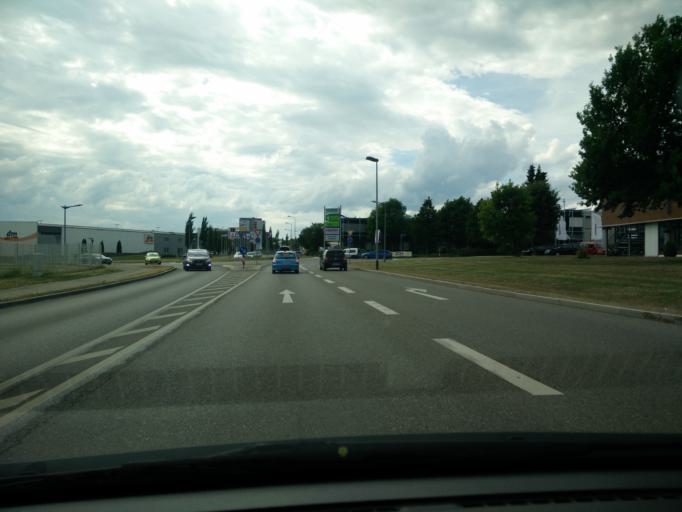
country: DE
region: Baden-Wuerttemberg
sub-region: Freiburg Region
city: Dauchingen
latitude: 48.0633
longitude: 8.5599
